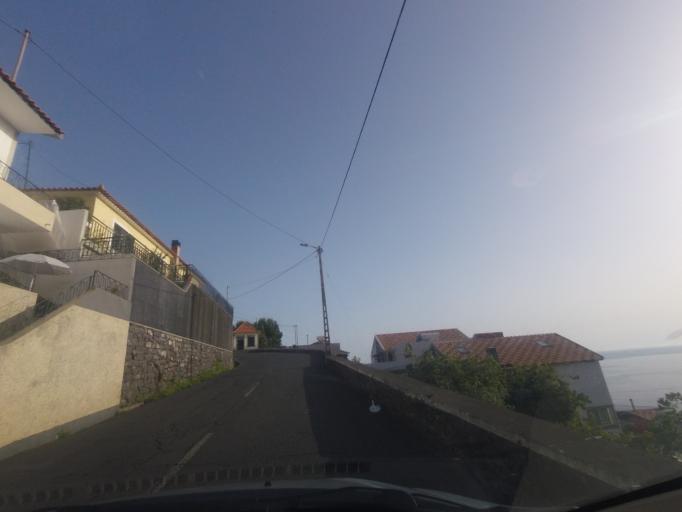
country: PT
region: Madeira
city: Ribeira Brava
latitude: 32.6763
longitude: -17.0669
